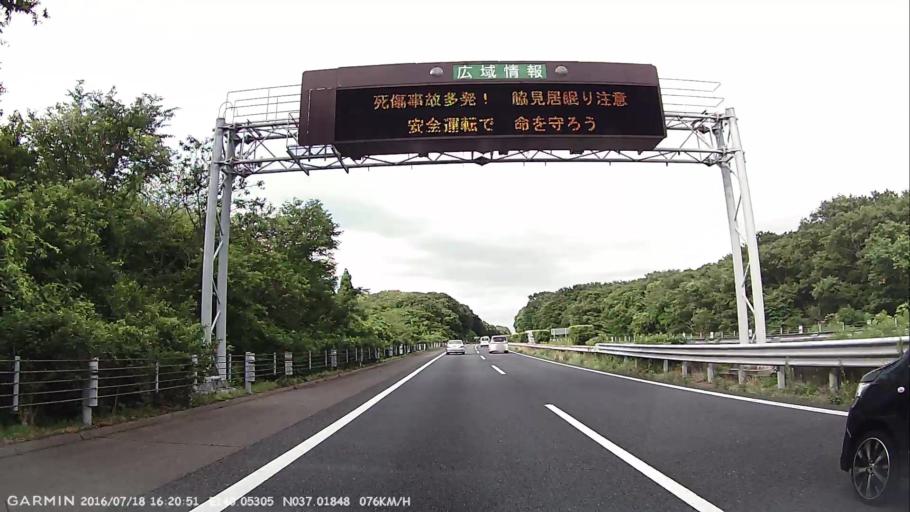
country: JP
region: Tochigi
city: Kuroiso
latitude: 37.0186
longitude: 140.0532
